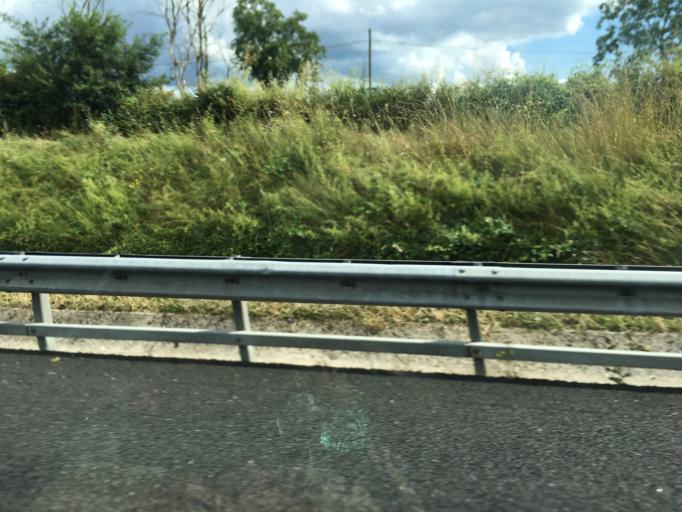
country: IT
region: Latium
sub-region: Citta metropolitana di Roma Capitale
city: Valmontone
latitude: 41.7621
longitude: 12.9429
